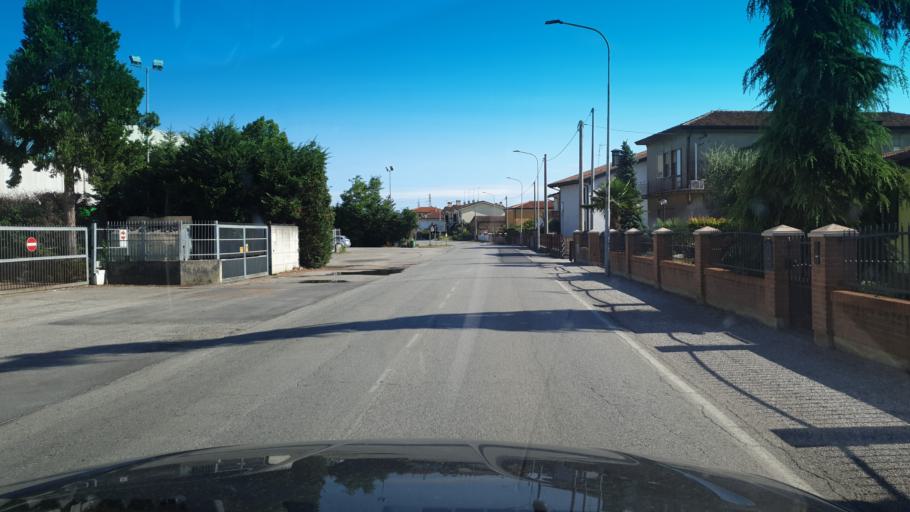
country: IT
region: Veneto
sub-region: Provincia di Rovigo
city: Rovigo
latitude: 45.0855
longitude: 11.7760
